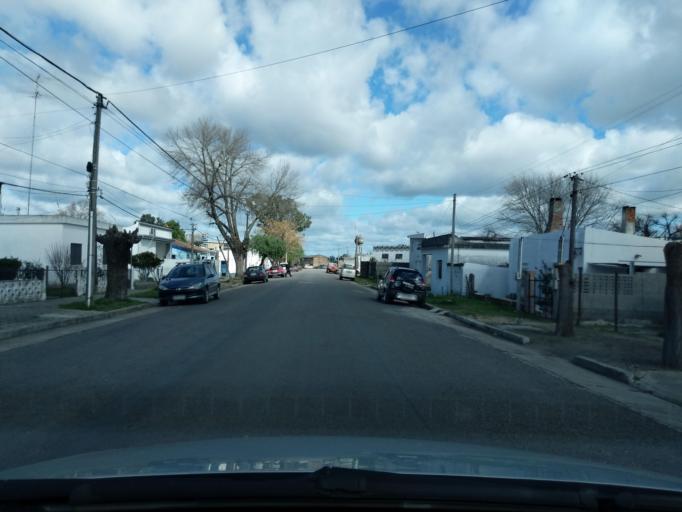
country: UY
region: Florida
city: Florida
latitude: -34.0844
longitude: -56.2228
